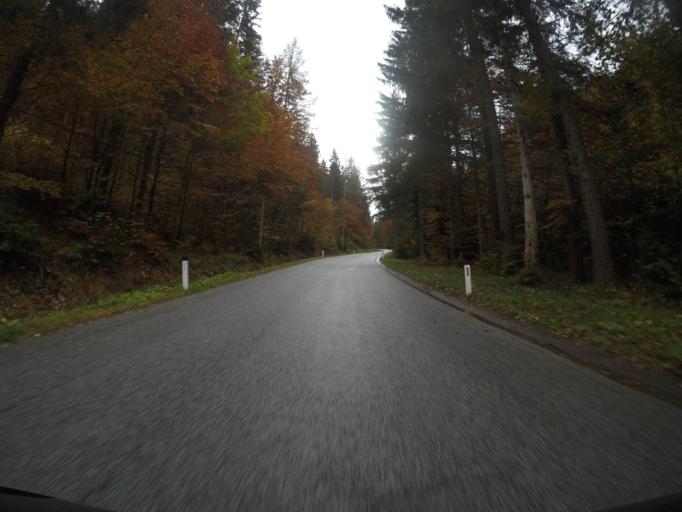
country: SI
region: Kranjska Gora
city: Mojstrana
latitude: 46.4464
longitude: 13.9326
